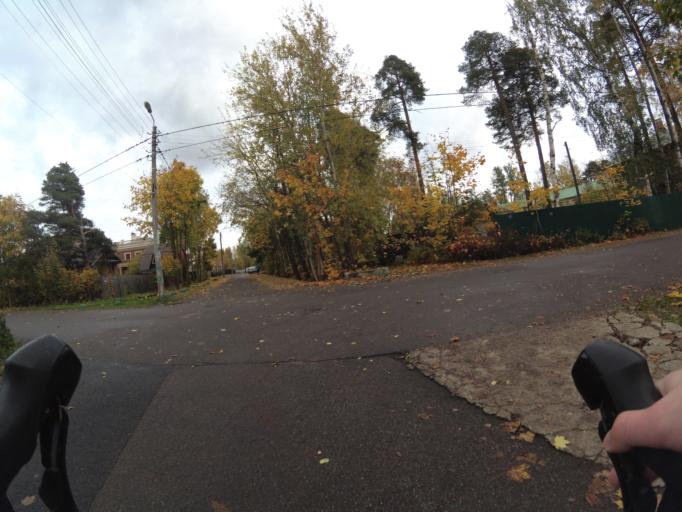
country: RU
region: St.-Petersburg
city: Lakhtinskiy
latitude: 59.9993
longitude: 30.1482
